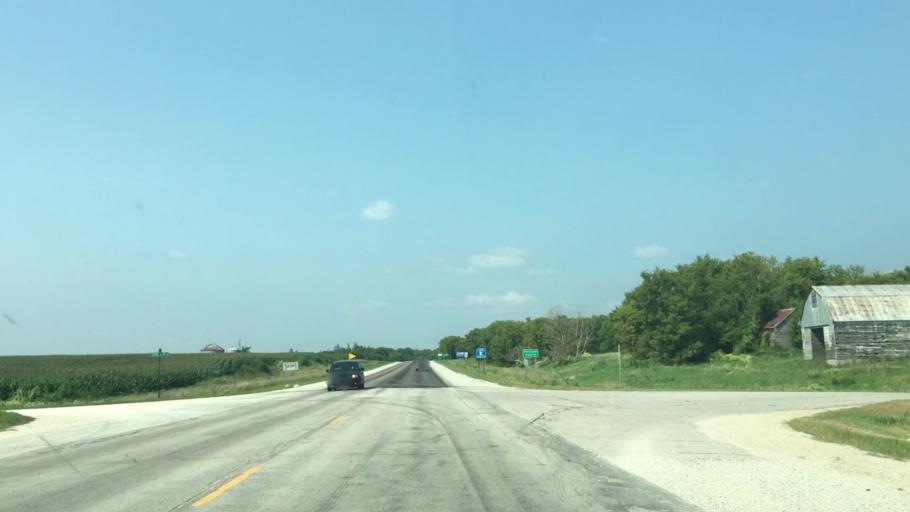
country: US
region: Minnesota
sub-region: Fillmore County
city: Harmony
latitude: 43.5005
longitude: -91.8711
